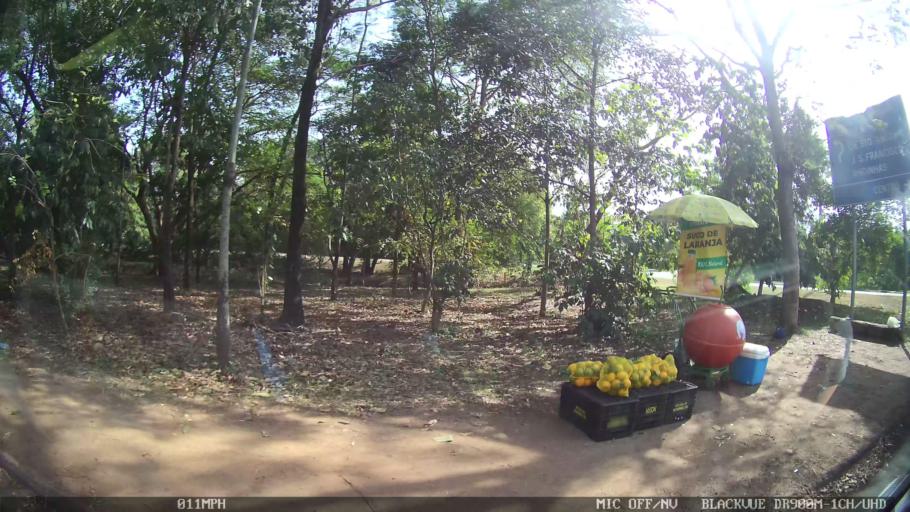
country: BR
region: Sao Paulo
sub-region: Piracicaba
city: Piracicaba
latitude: -22.7251
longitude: -47.6706
